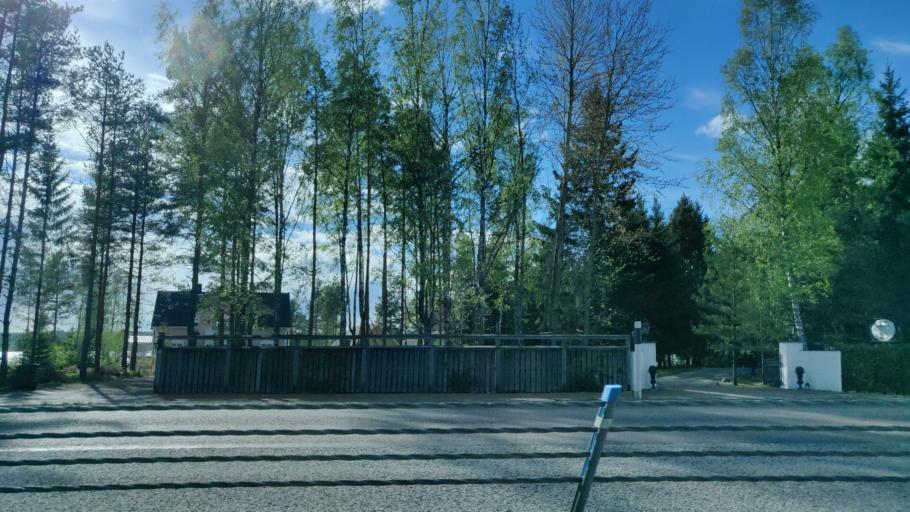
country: SE
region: Vaermland
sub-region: Forshaga Kommun
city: Forshaga
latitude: 59.4792
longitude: 13.4110
